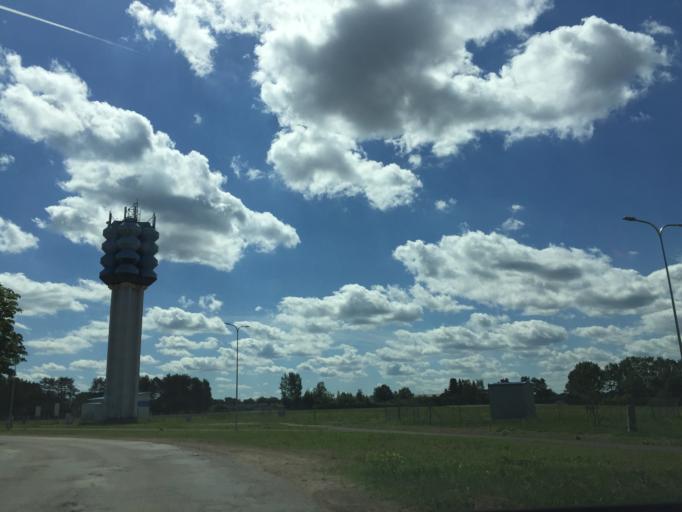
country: LV
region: Babite
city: Pinki
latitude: 56.8780
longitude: 23.9475
